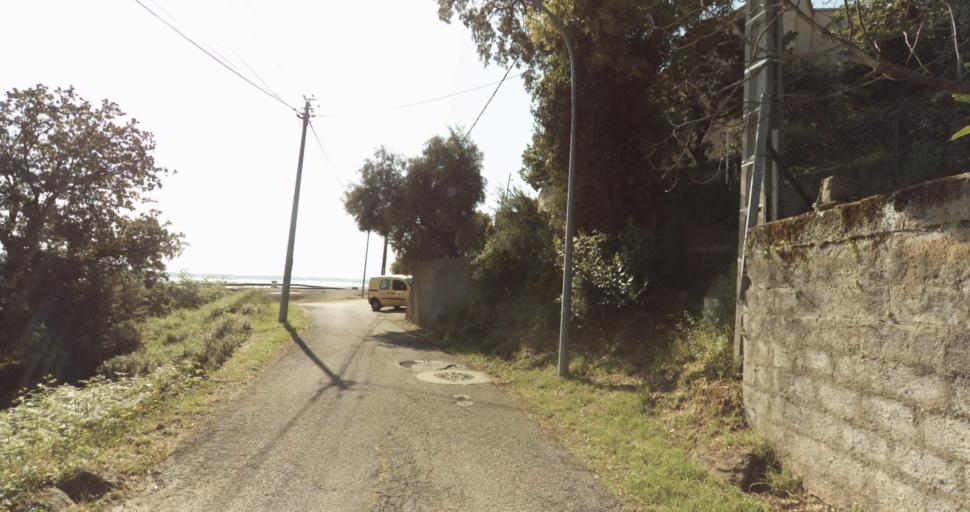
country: FR
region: Corsica
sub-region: Departement de la Haute-Corse
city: Biguglia
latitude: 42.6303
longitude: 9.4180
